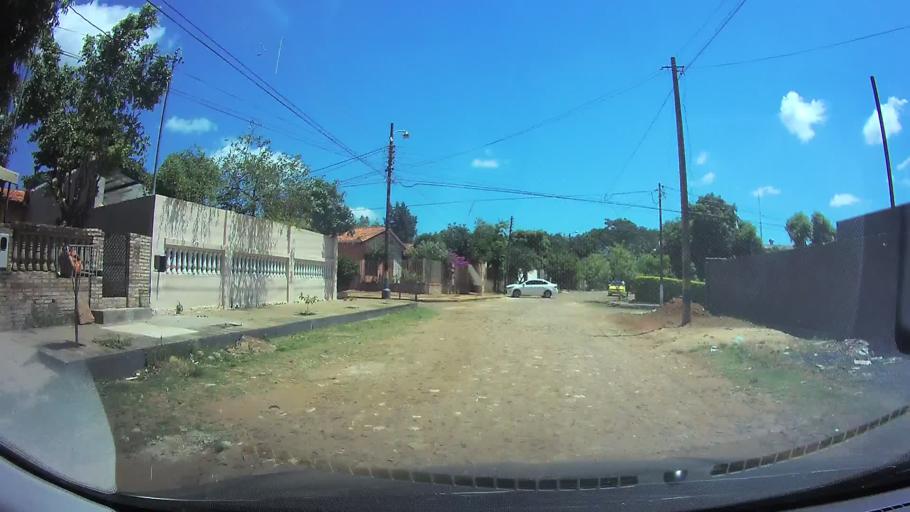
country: PY
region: Central
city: San Lorenzo
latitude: -25.2619
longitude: -57.4855
